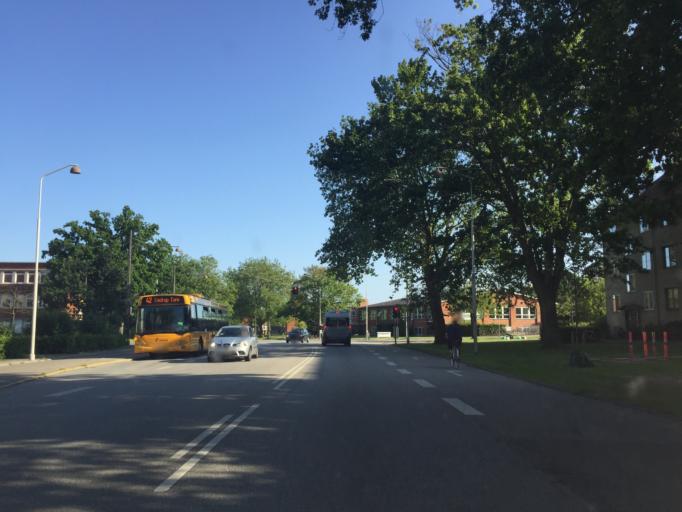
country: DK
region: Capital Region
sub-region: Frederiksberg Kommune
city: Frederiksberg
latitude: 55.7161
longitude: 12.5456
